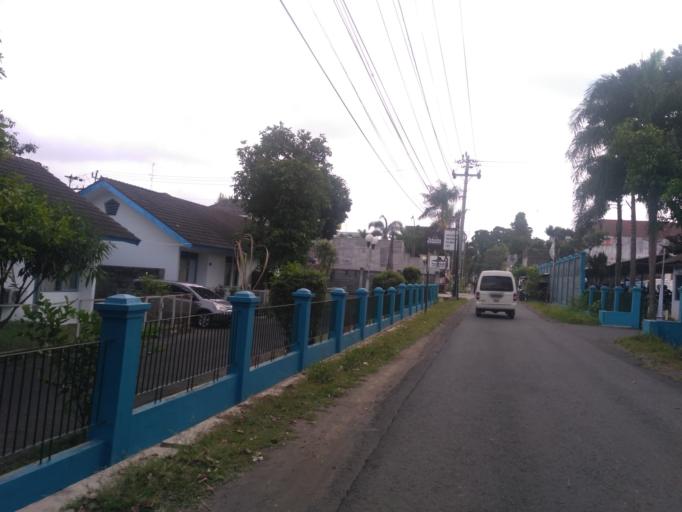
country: ID
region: Daerah Istimewa Yogyakarta
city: Melati
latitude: -7.7510
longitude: 110.3606
